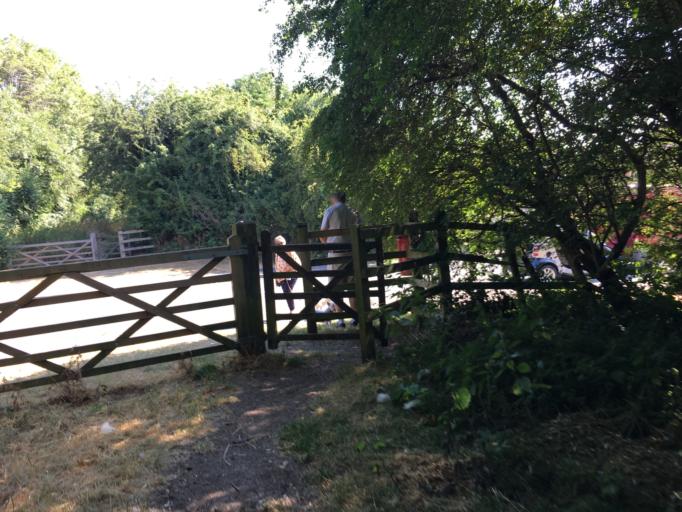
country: GB
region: England
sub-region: Warwickshire
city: Rugby
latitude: 52.3908
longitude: -1.2366
